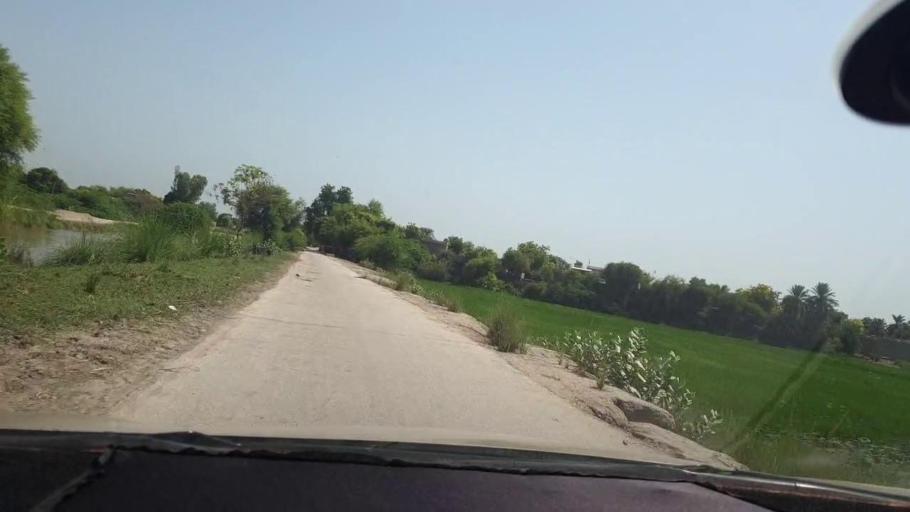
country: PK
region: Sindh
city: Kambar
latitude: 27.5092
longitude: 68.0122
